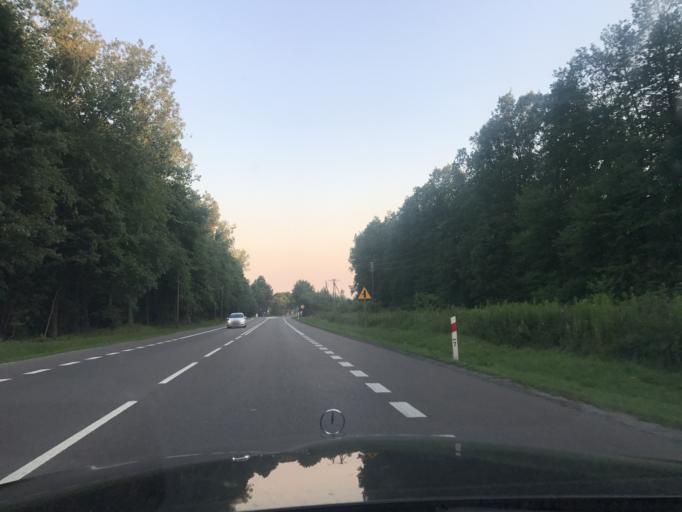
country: PL
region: Lublin Voivodeship
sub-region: Powiat lubelski
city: Niemce
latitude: 51.3775
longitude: 22.6346
